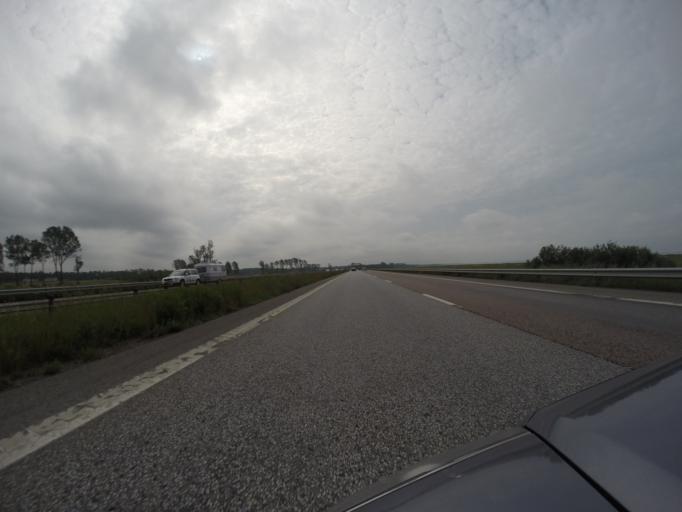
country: SE
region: Skane
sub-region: Landskrona
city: Asmundtorp
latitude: 55.8497
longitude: 12.9002
